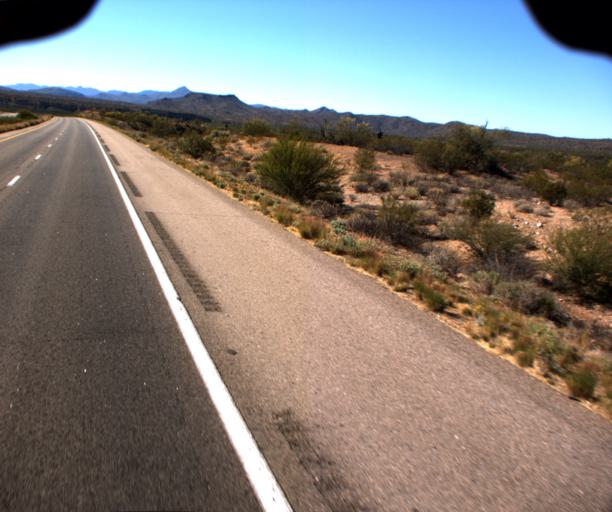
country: US
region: Arizona
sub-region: Yavapai County
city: Bagdad
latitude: 34.6502
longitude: -113.5719
